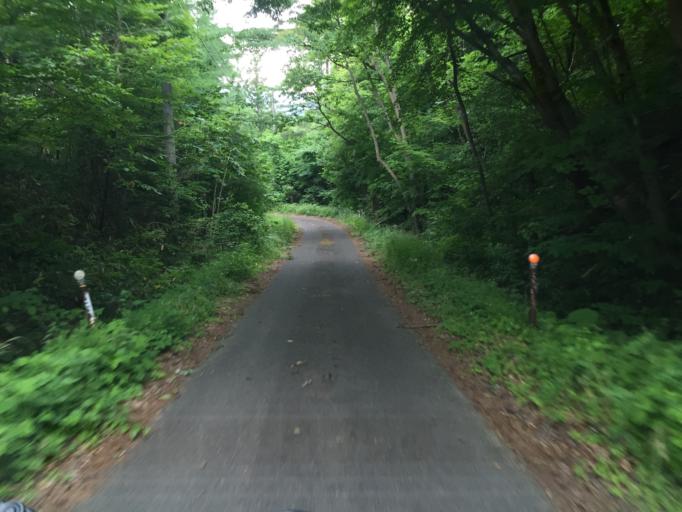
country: JP
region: Fukushima
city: Fukushima-shi
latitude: 37.7201
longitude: 140.3363
